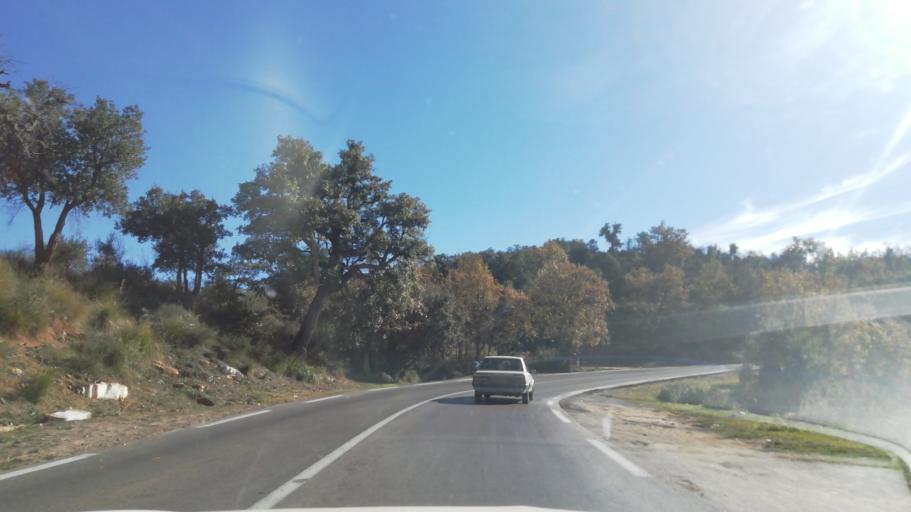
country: DZ
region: Tlemcen
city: Mansoura
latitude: 34.8399
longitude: -1.3687
